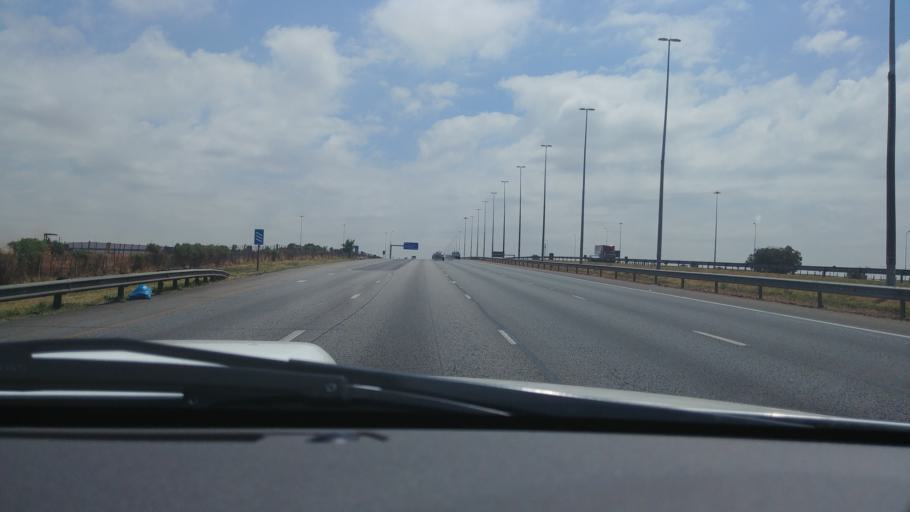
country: ZA
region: Gauteng
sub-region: Ekurhuleni Metropolitan Municipality
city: Tembisa
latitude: -26.0343
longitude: 28.2682
